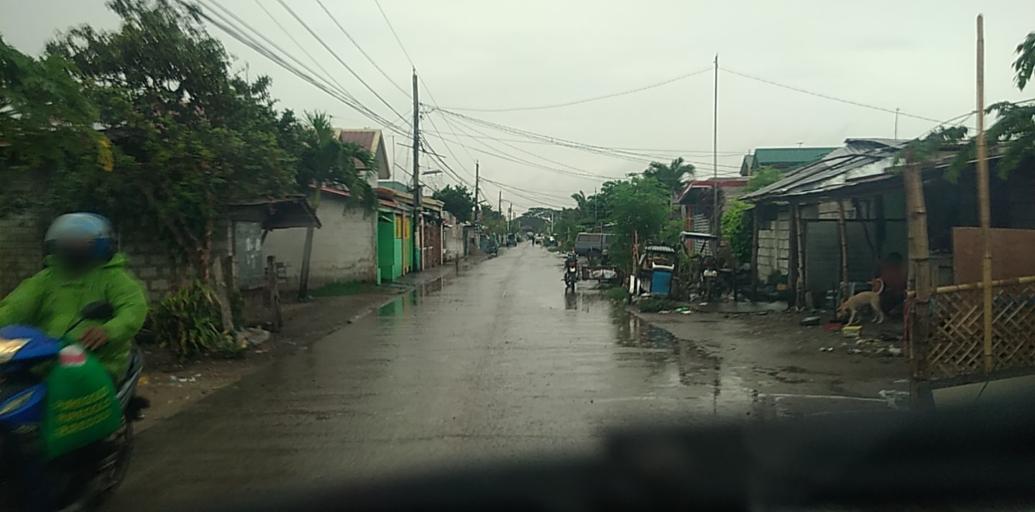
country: PH
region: Central Luzon
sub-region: Province of Pampanga
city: San Antonio
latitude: 15.1619
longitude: 120.6919
